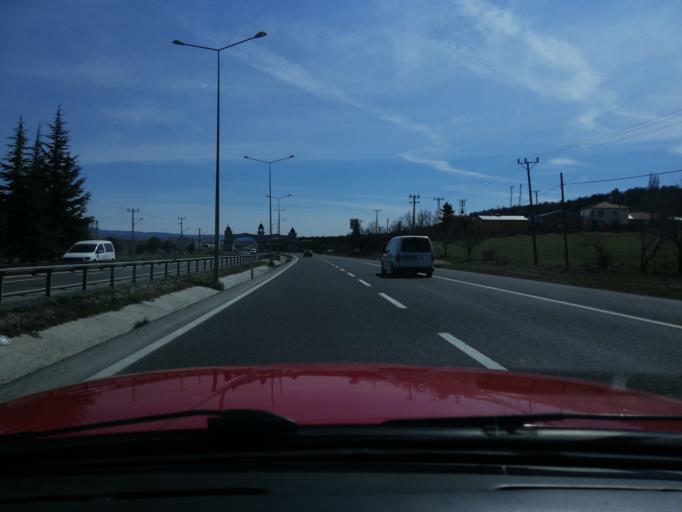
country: TR
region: Kuetahya
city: Kutahya
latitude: 39.3772
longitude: 30.0530
